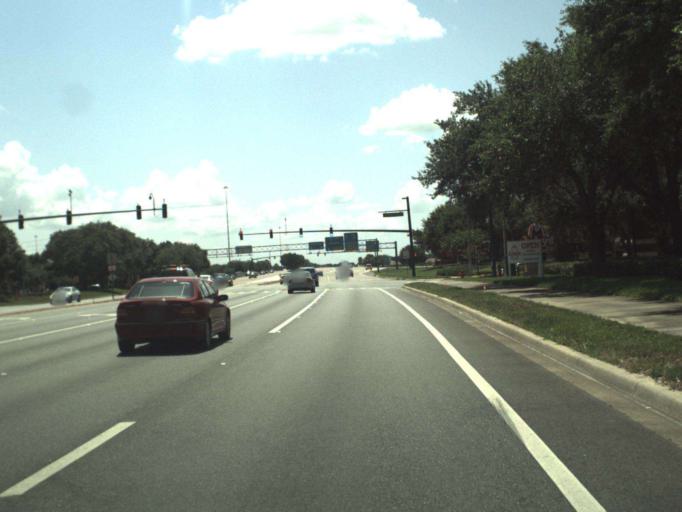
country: US
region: Florida
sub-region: Seminole County
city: Heathrow
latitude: 28.7564
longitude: -81.3568
